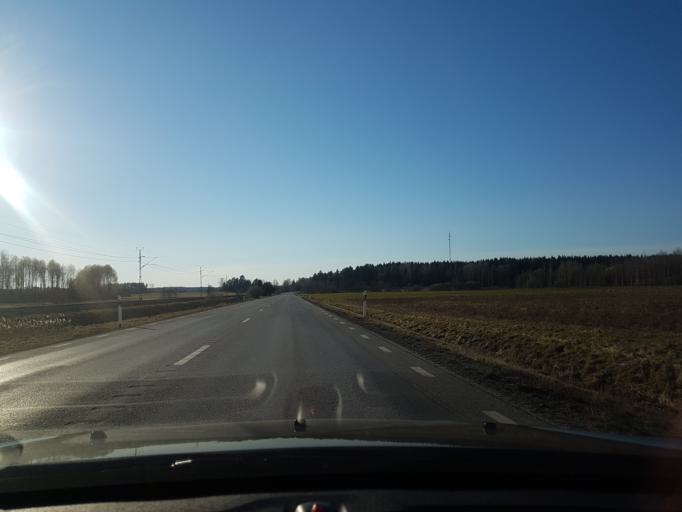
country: SE
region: Uppsala
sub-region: Heby Kommun
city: Morgongava
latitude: 59.9078
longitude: 17.0424
